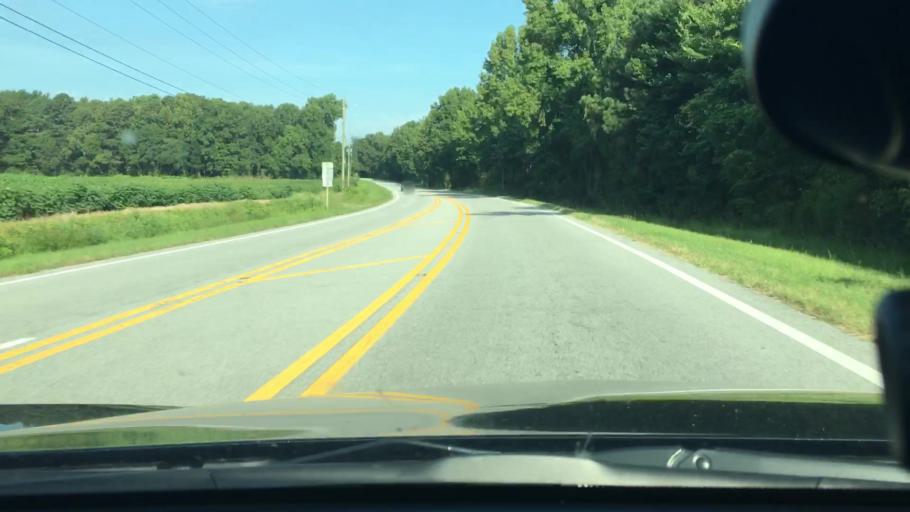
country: US
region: North Carolina
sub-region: Pitt County
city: Farmville
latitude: 35.6939
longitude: -77.4995
